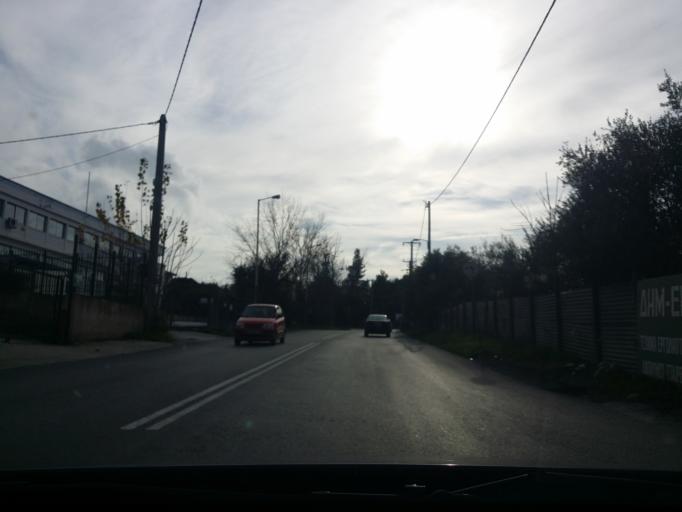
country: GR
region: Attica
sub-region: Nomarchia Athinas
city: Metamorfosi
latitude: 38.0738
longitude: 23.7604
